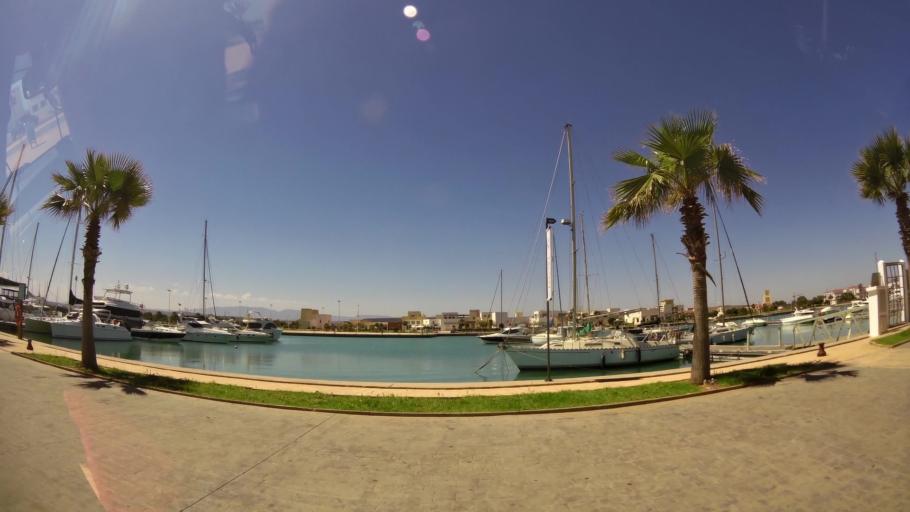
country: MA
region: Oriental
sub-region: Berkane-Taourirt
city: Madagh
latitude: 35.1107
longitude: -2.2955
